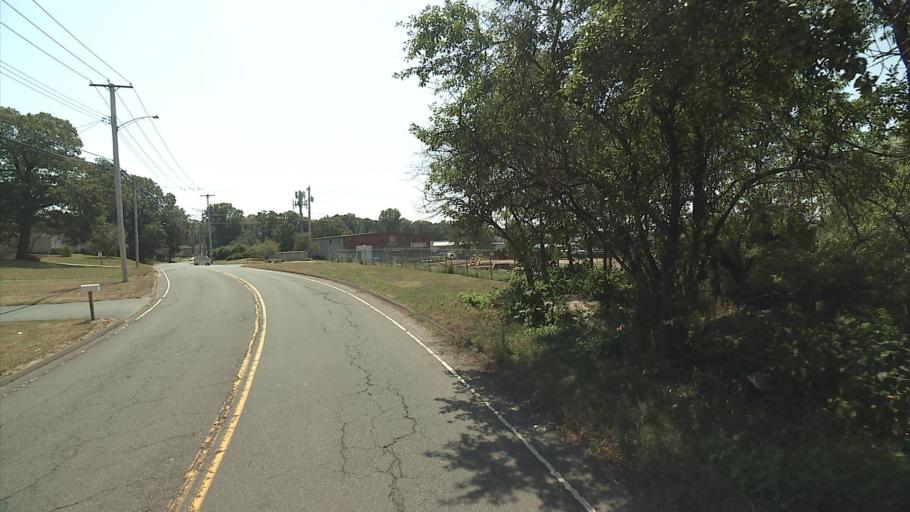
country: US
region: Connecticut
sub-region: New Haven County
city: East Haven
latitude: 41.2574
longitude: -72.8760
